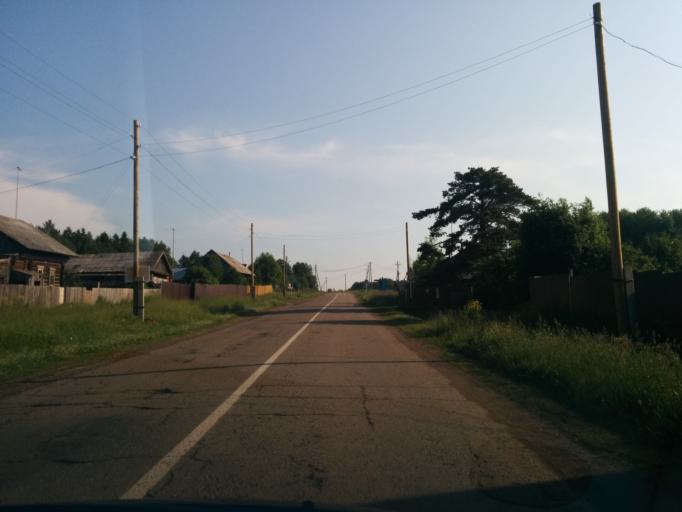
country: RU
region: Perm
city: Polazna
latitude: 58.2448
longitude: 56.2678
